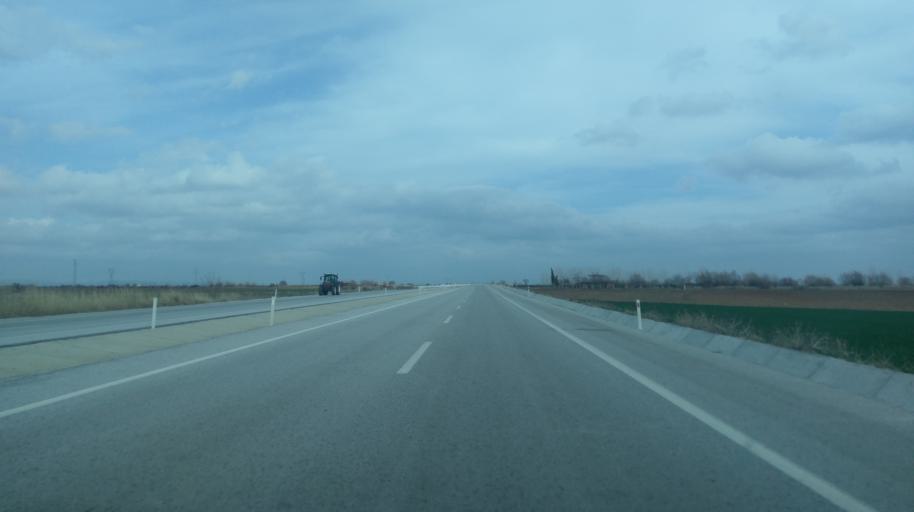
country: TR
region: Kirklareli
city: Inece
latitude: 41.6816
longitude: 27.1085
